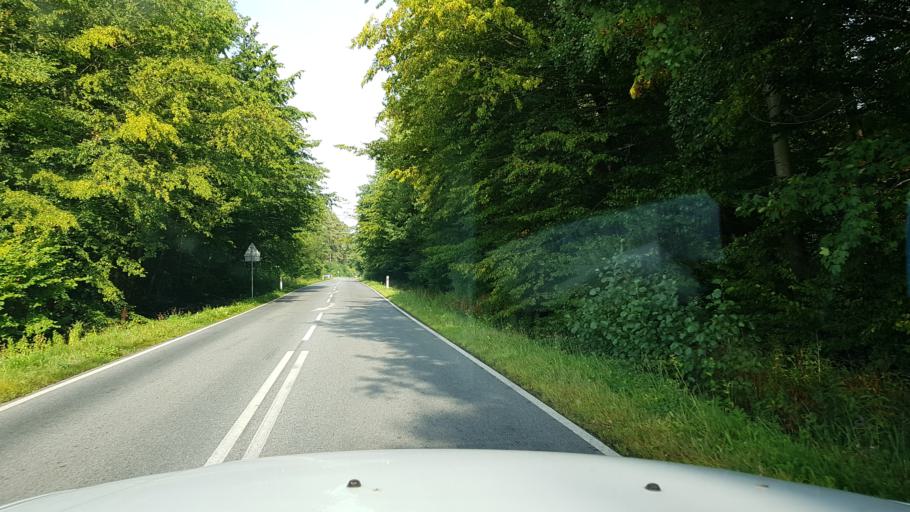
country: PL
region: West Pomeranian Voivodeship
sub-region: Powiat slawienski
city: Slawno
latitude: 54.3772
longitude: 16.6302
